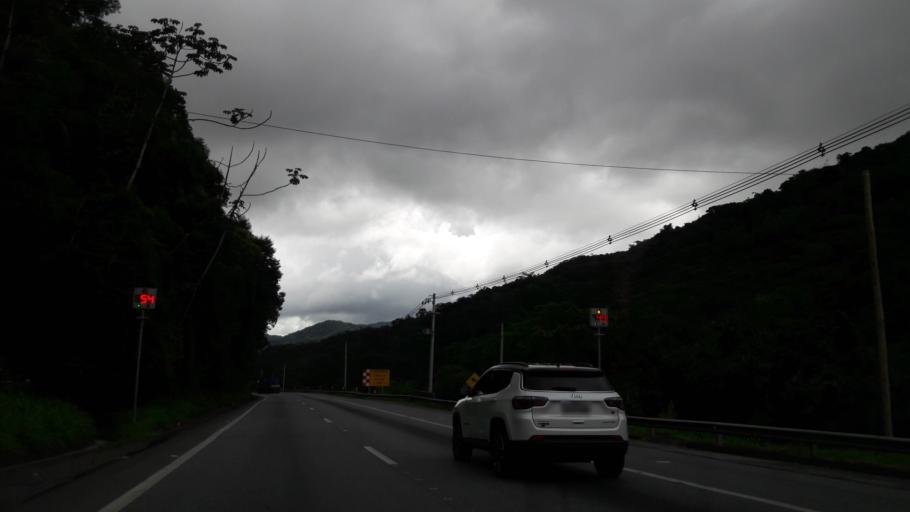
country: BR
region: Sao Paulo
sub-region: Juquitiba
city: Juquitiba
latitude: -24.0653
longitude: -47.2343
